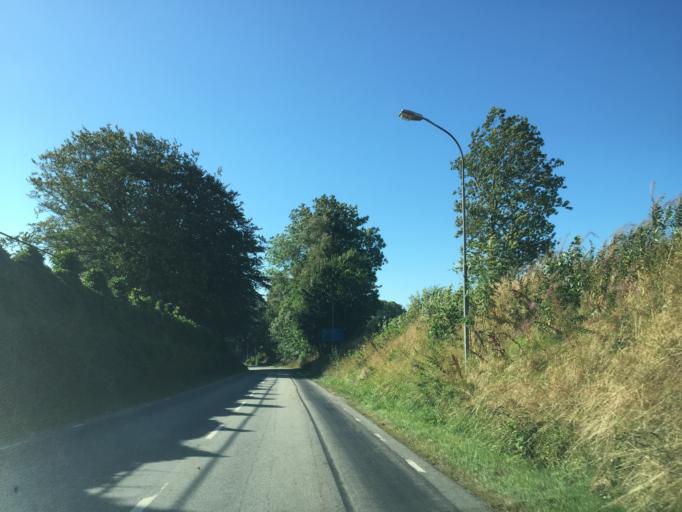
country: SE
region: Skane
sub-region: Ystads Kommun
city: Kopingebro
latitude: 55.4455
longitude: 14.1213
